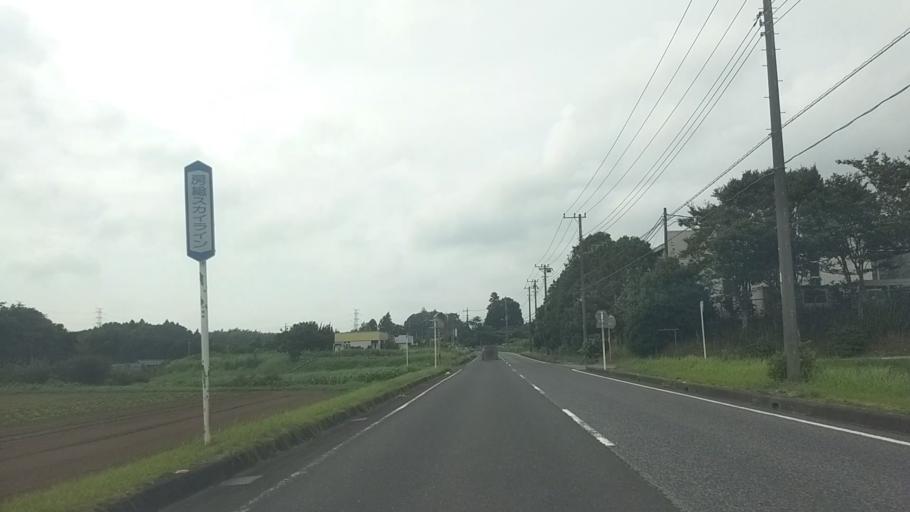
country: JP
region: Chiba
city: Kimitsu
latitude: 35.2753
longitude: 139.9943
